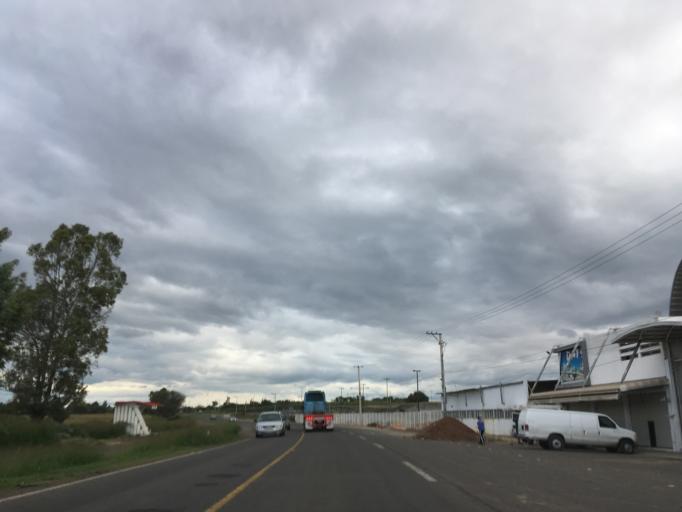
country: MX
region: Michoacan
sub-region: Cuitzeo
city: Cuamio
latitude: 20.0705
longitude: -101.1554
